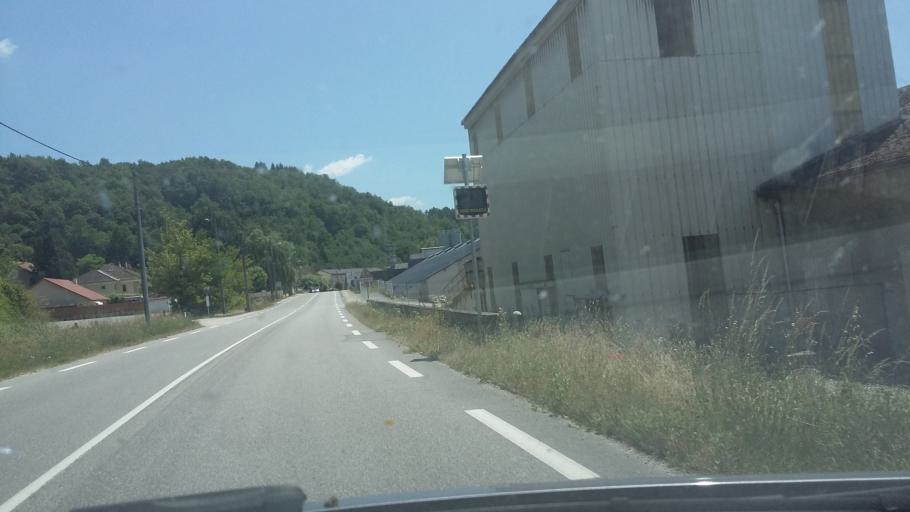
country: FR
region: Rhone-Alpes
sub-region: Departement de l'Ain
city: Belley
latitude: 45.8083
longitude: 5.6809
